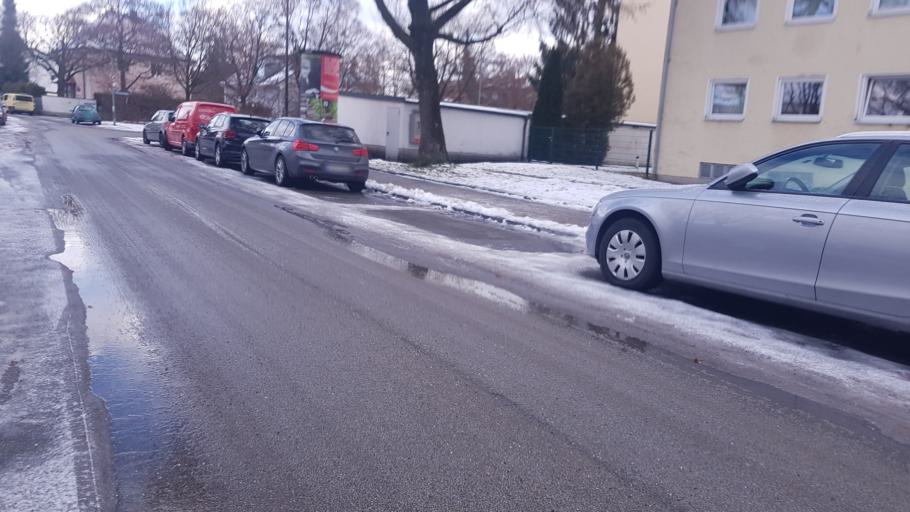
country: DE
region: Bavaria
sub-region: Upper Bavaria
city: Bogenhausen
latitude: 48.1266
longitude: 11.6485
